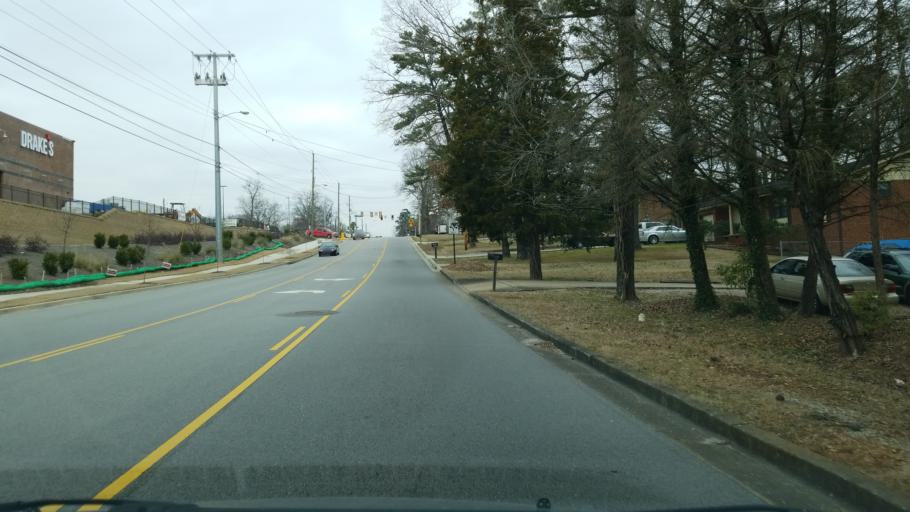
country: US
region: Tennessee
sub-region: Hamilton County
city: East Brainerd
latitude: 35.0418
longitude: -85.1492
